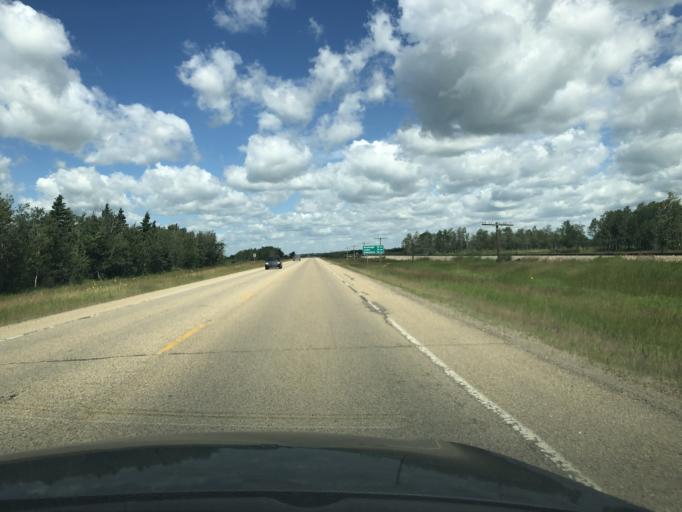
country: CA
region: Alberta
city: Millet
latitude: 53.1012
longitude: -113.4741
